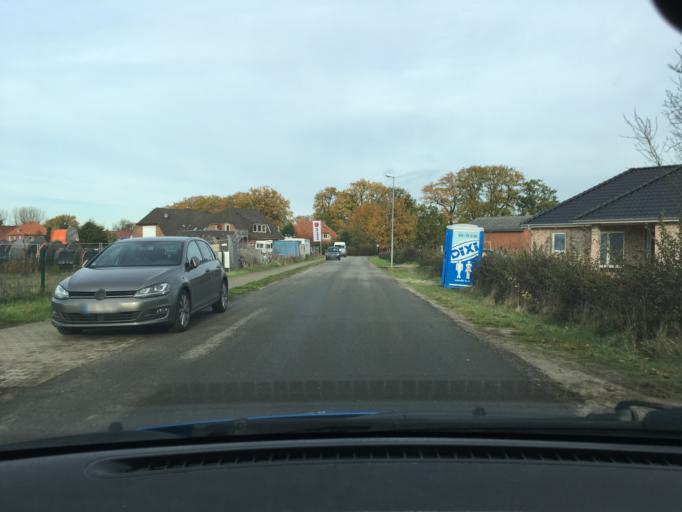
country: DE
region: Lower Saxony
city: Wittorf
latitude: 53.3285
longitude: 10.3797
